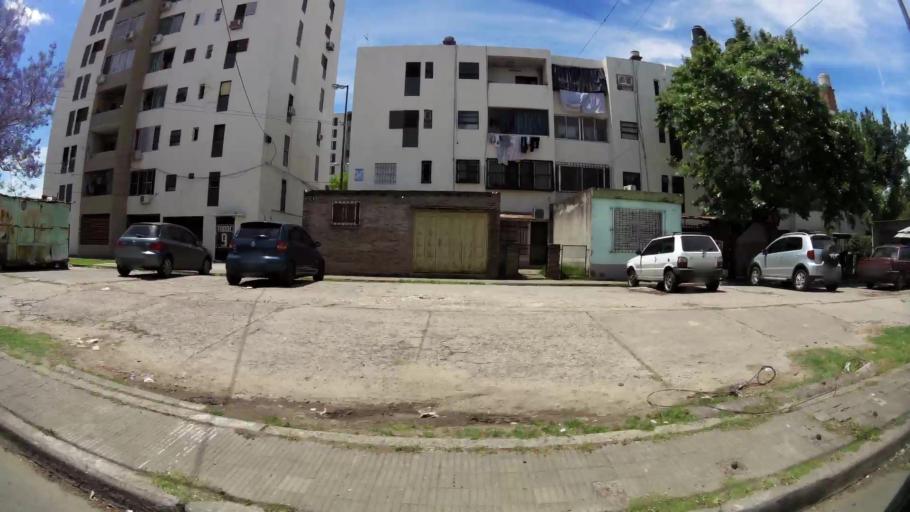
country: AR
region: Santa Fe
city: Gobernador Galvez
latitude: -32.9918
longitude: -60.6248
